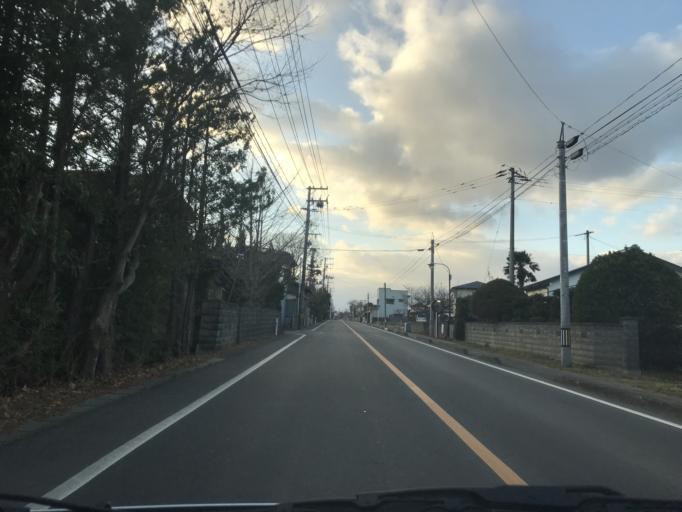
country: JP
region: Miyagi
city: Furukawa
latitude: 38.6586
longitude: 141.0172
